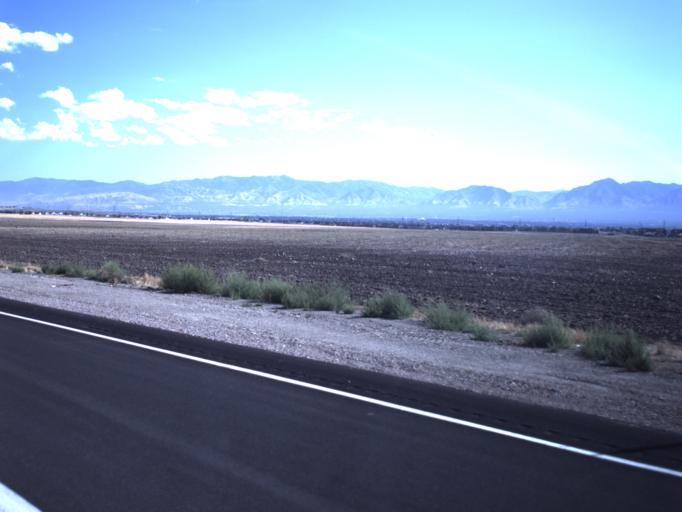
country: US
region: Utah
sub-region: Salt Lake County
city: Oquirrh
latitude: 40.5768
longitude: -112.0615
